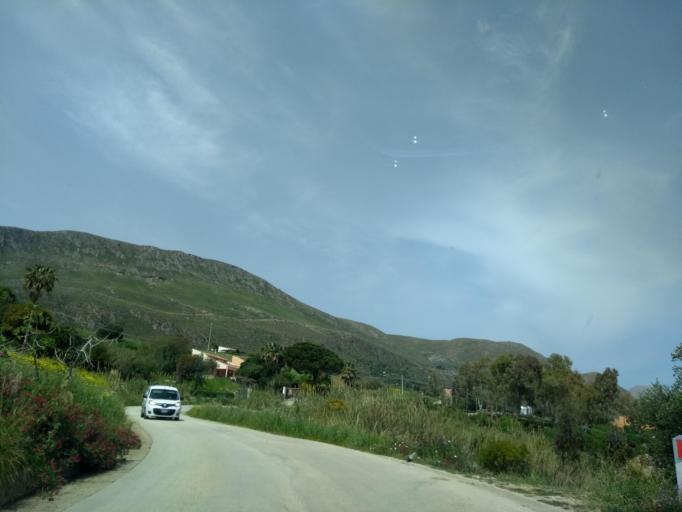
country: IT
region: Sicily
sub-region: Trapani
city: Castelluzzo
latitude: 38.0728
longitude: 12.8187
